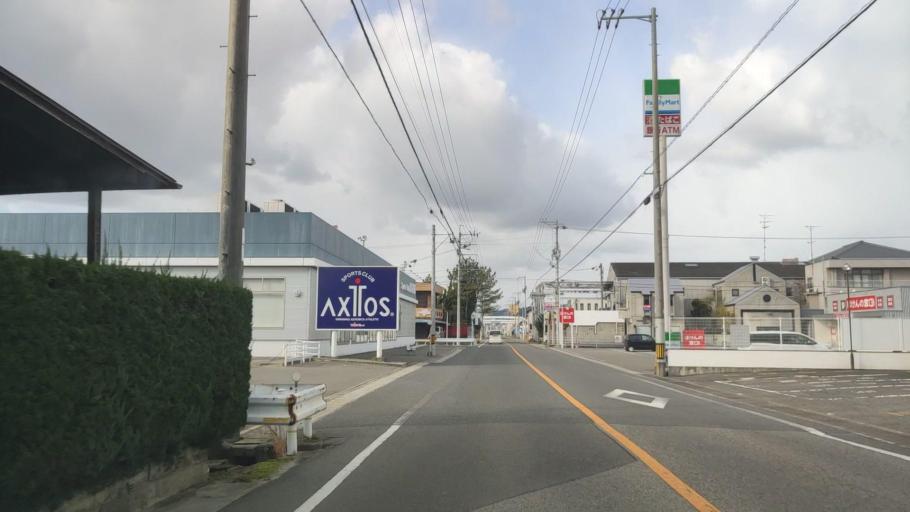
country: JP
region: Ehime
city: Saijo
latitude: 34.0489
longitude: 133.0163
